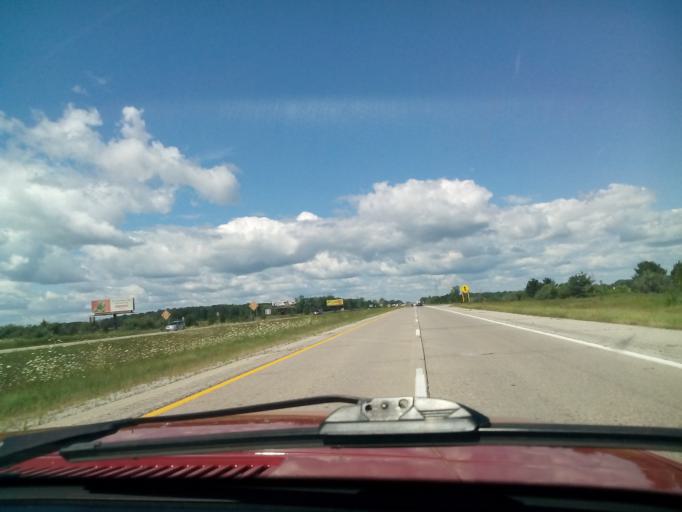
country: US
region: Michigan
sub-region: Bay County
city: Bay City
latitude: 43.6248
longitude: -83.9554
